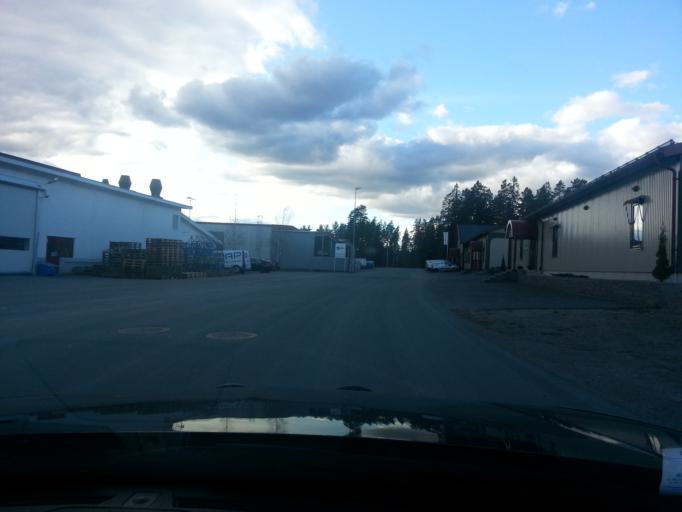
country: SE
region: Joenkoeping
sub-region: Vetlanda Kommun
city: Vetlanda
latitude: 57.4132
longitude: 15.0645
